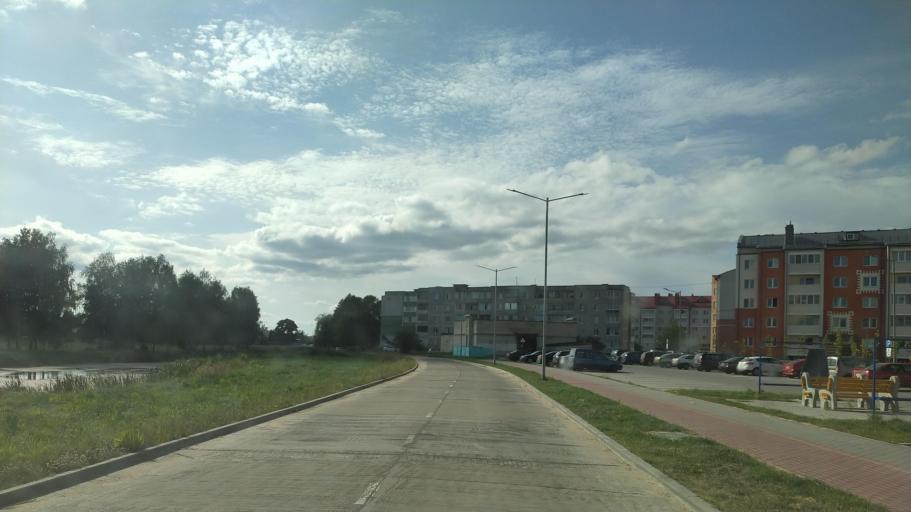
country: BY
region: Brest
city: Byaroza
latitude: 52.5357
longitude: 24.9938
